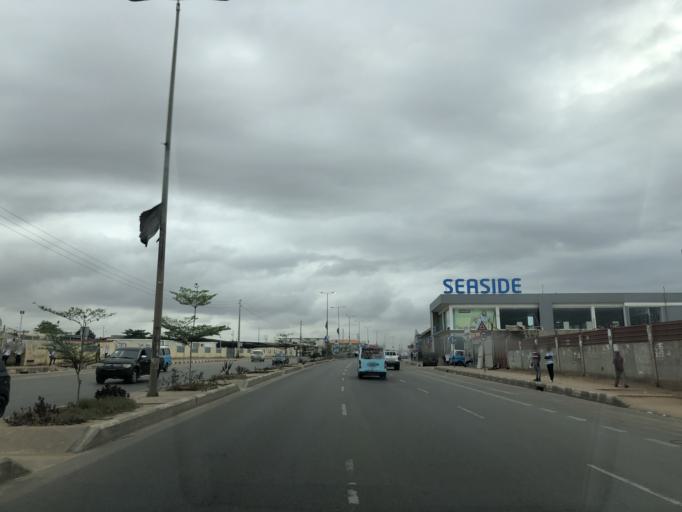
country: AO
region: Luanda
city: Luanda
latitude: -8.8787
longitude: 13.2097
